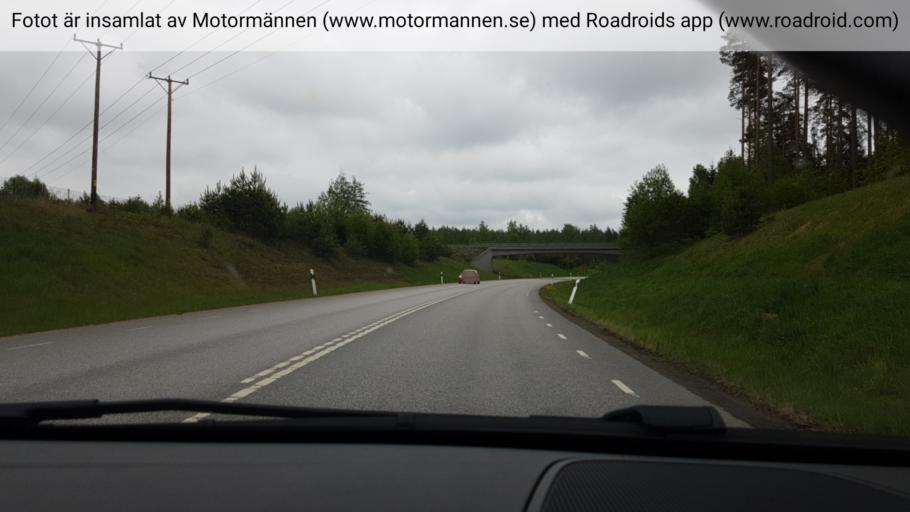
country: SE
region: Uppsala
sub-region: Osthammars Kommun
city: Bjorklinge
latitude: 60.0189
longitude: 17.5805
